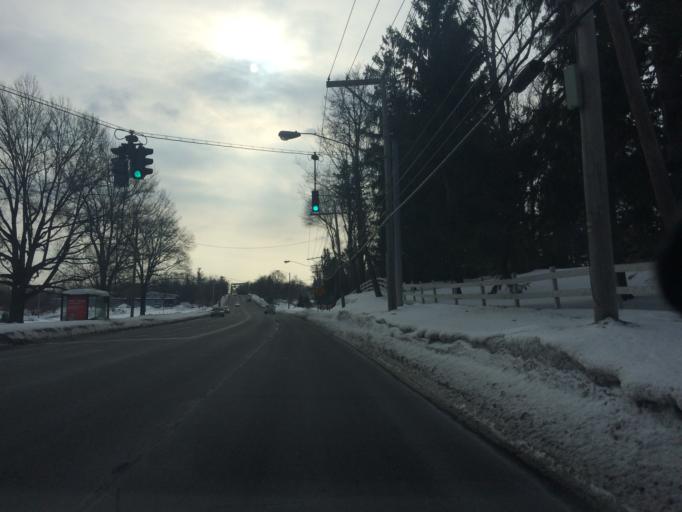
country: US
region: New York
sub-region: Monroe County
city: Pittsford
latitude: 43.0959
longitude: -77.5277
